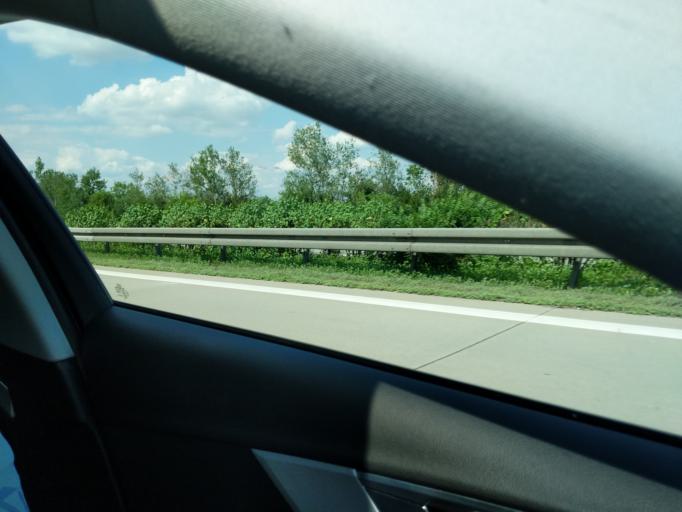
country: DE
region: Saxony
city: Wiedemar
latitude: 51.4854
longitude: 12.2099
